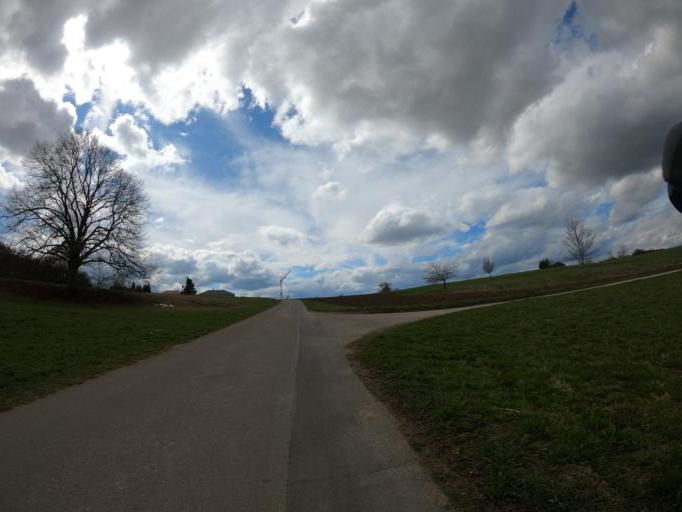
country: DE
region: Baden-Wuerttemberg
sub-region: Tuebingen Region
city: Pfullingen
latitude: 48.3906
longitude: 9.1915
